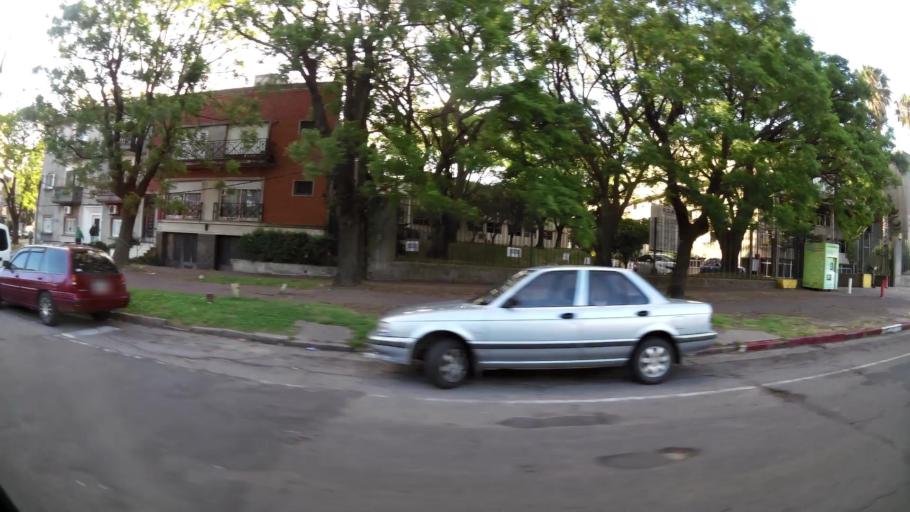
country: UY
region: Montevideo
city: Montevideo
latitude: -34.8852
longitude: -56.1529
